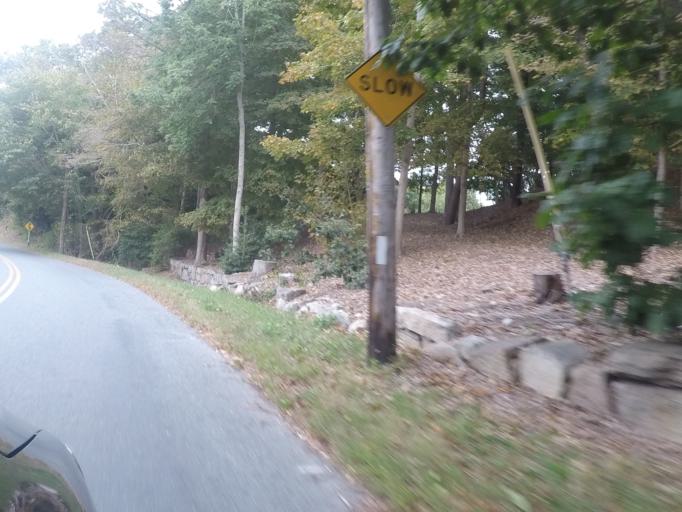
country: US
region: Massachusetts
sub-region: Bristol County
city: Smith Mills
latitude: 41.5709
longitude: -71.0061
